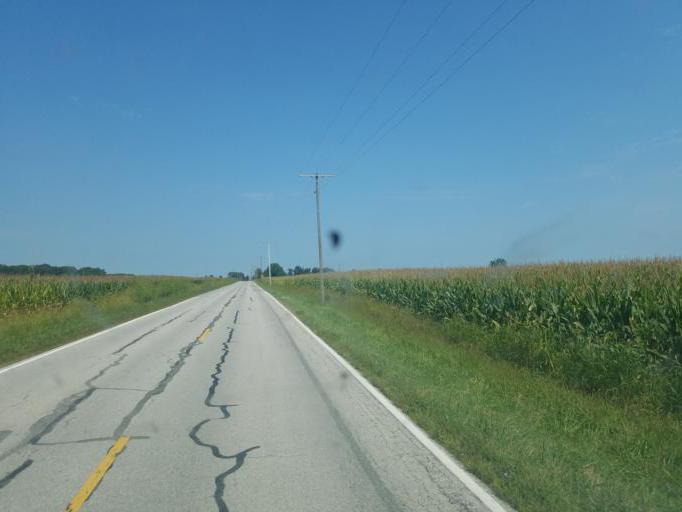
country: US
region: Ohio
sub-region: Marion County
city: Marion
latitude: 40.6265
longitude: -83.2173
